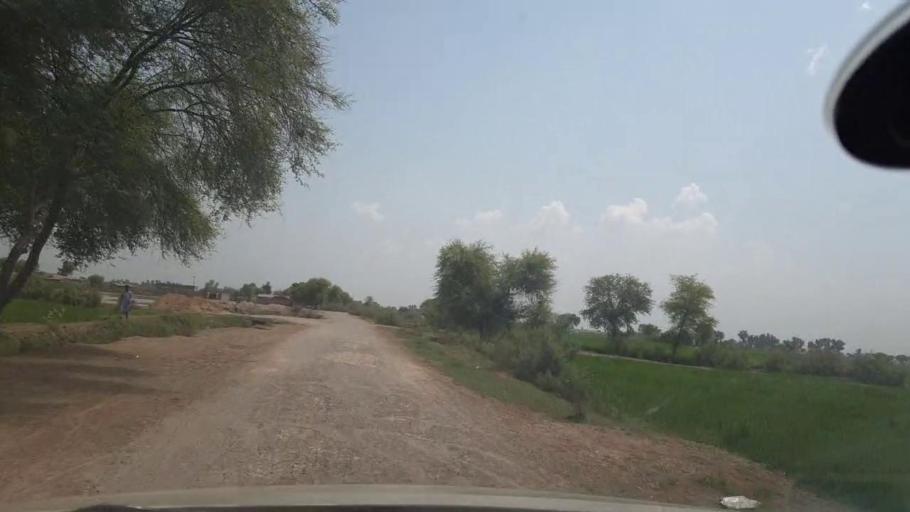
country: PK
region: Sindh
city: Jacobabad
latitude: 28.1299
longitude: 68.3807
